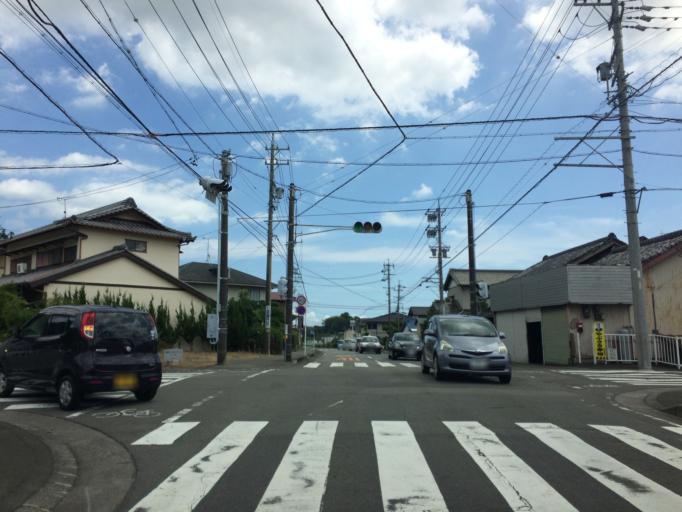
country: JP
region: Shizuoka
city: Yaizu
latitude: 34.9024
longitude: 138.2958
